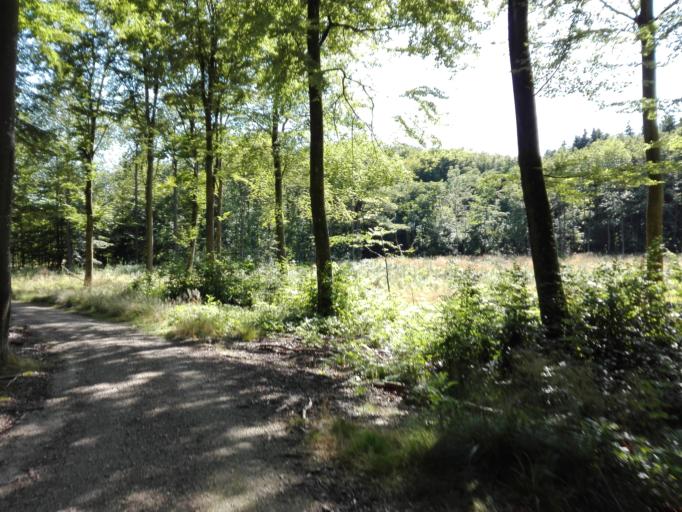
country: DK
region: Central Jutland
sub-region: Odder Kommune
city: Odder
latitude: 55.9708
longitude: 10.1201
